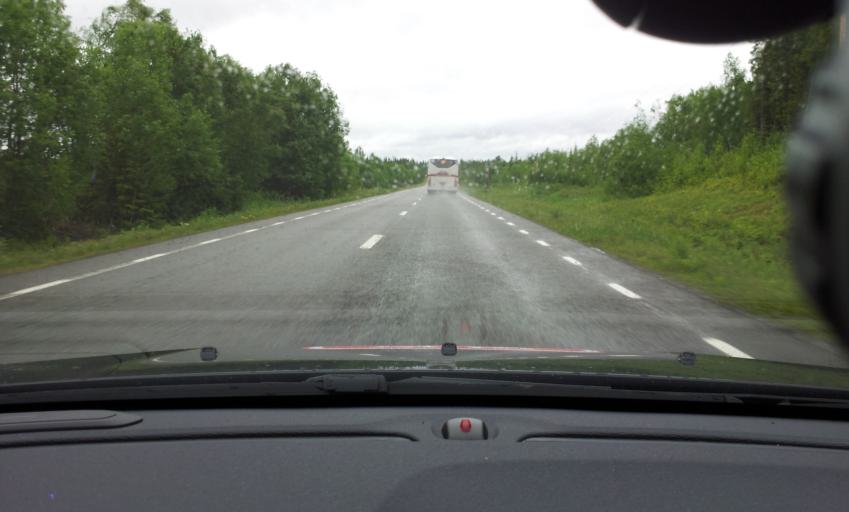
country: SE
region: Jaemtland
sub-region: Krokoms Kommun
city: Krokom
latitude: 63.5653
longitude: 14.6142
